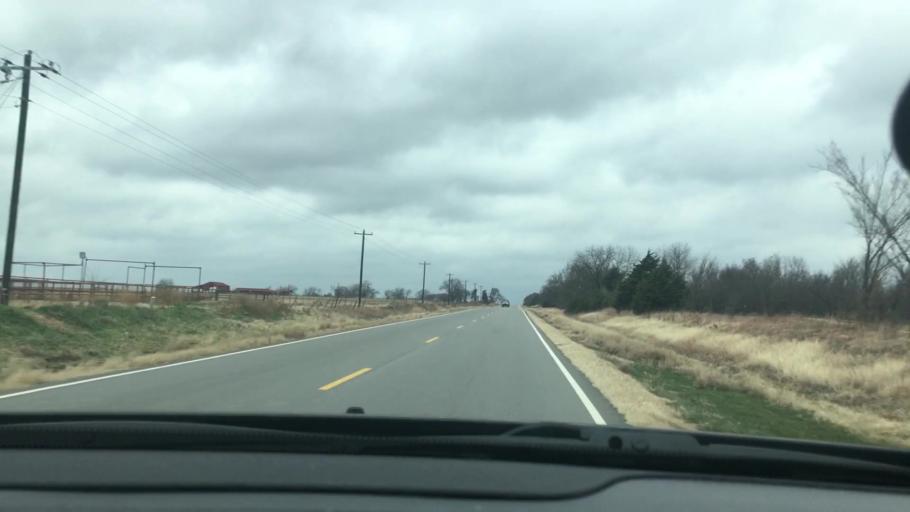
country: US
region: Oklahoma
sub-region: Atoka County
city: Atoka
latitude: 34.3749
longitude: -96.2418
